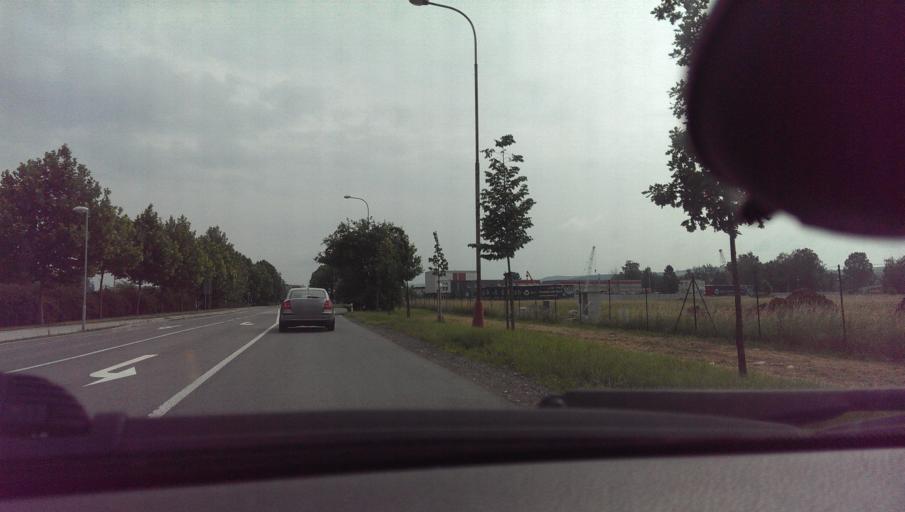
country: CZ
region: Zlin
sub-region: Okres Zlin
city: Otrokovice
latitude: 49.1984
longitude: 17.5245
